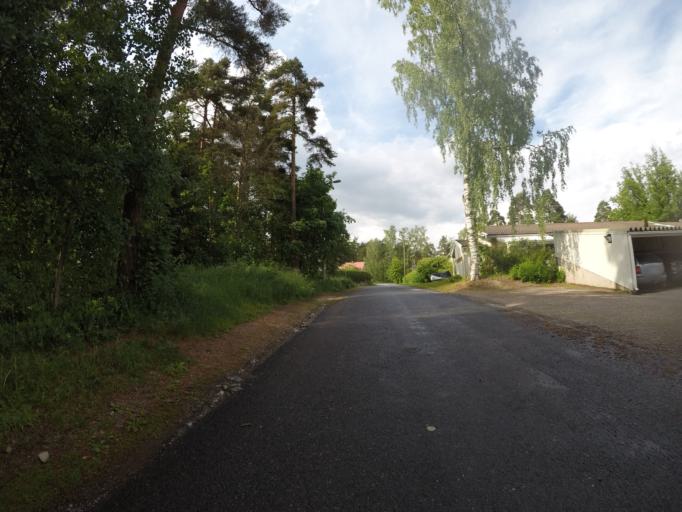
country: FI
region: Haeme
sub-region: Haemeenlinna
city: Haemeenlinna
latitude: 61.0068
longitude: 24.4730
